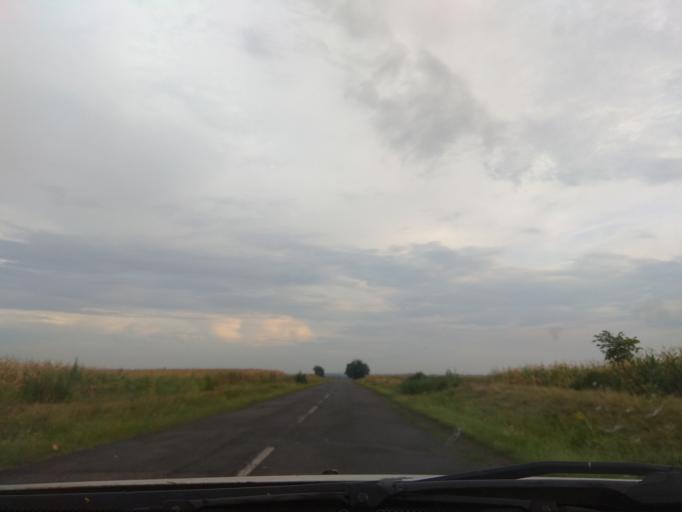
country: HU
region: Borsod-Abauj-Zemplen
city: Gesztely
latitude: 48.1171
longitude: 20.9726
